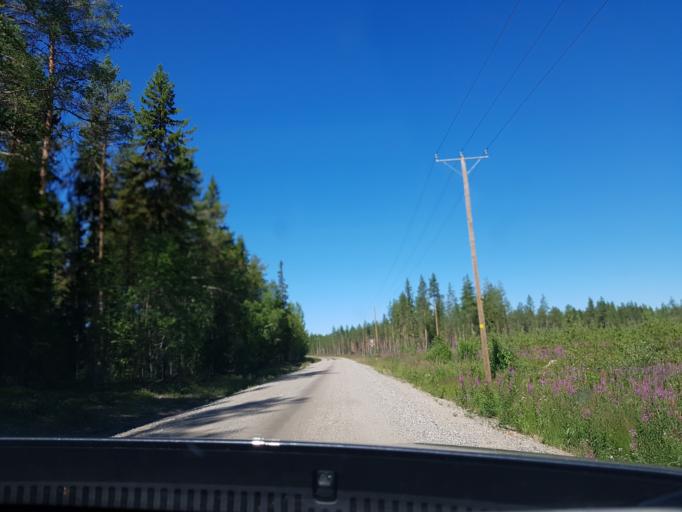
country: FI
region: Kainuu
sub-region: Kehys-Kainuu
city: Kuhmo
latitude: 64.1805
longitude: 29.6008
